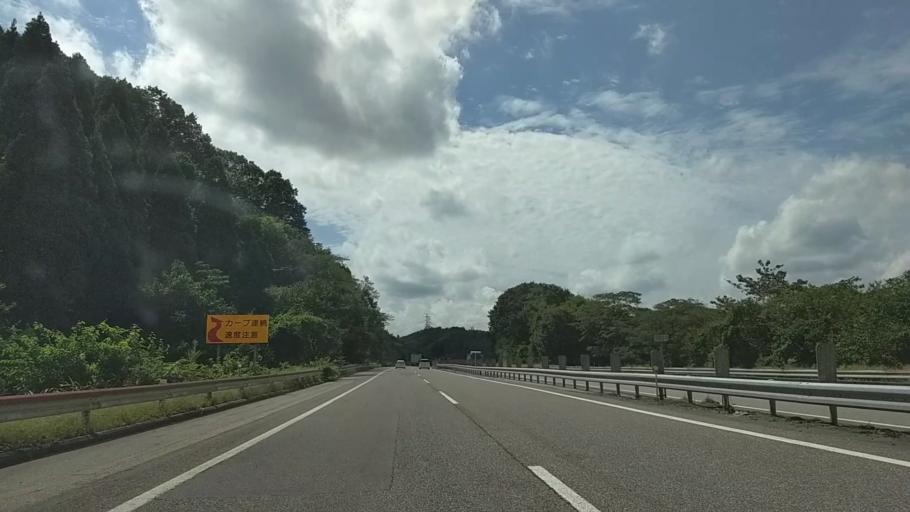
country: JP
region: Toyama
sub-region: Oyabe Shi
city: Oyabe
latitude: 36.6111
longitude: 136.8116
